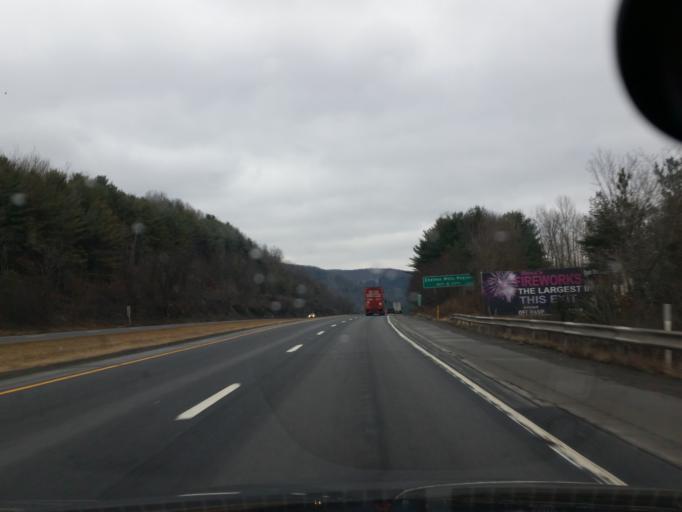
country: US
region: Pennsylvania
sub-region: Susquehanna County
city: Hallstead
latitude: 41.9751
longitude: -75.7417
